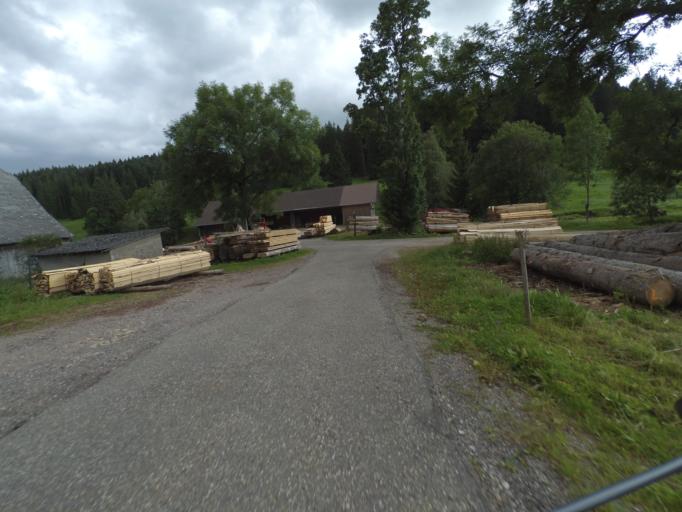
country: DE
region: Baden-Wuerttemberg
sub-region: Freiburg Region
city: Breitnau
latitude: 47.9563
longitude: 8.1326
